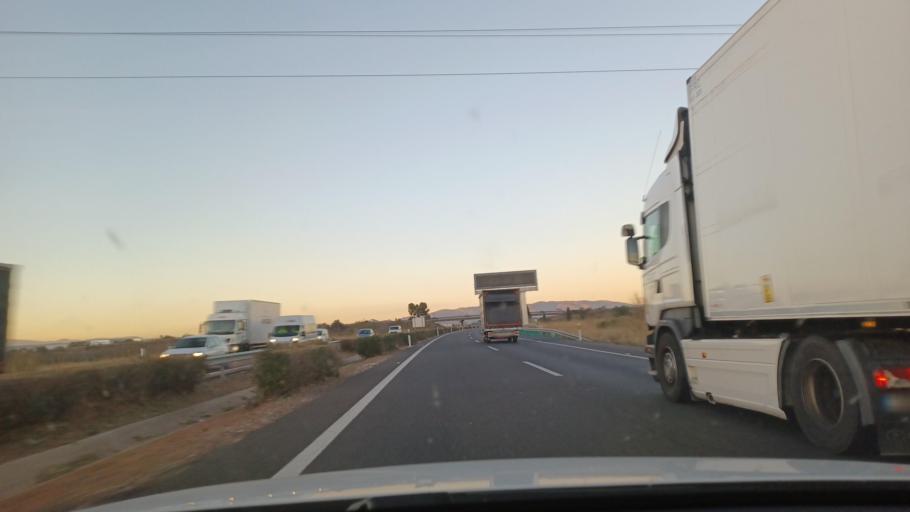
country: ES
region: Valencia
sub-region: Provincia de Castello
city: Vila-real
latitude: 39.9413
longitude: -0.1333
